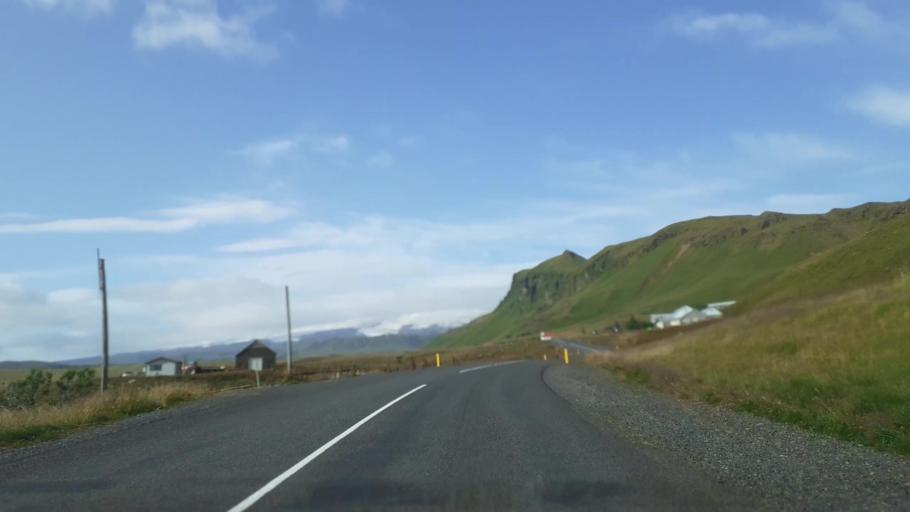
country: IS
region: South
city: Vestmannaeyjar
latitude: 63.4126
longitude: -19.0483
